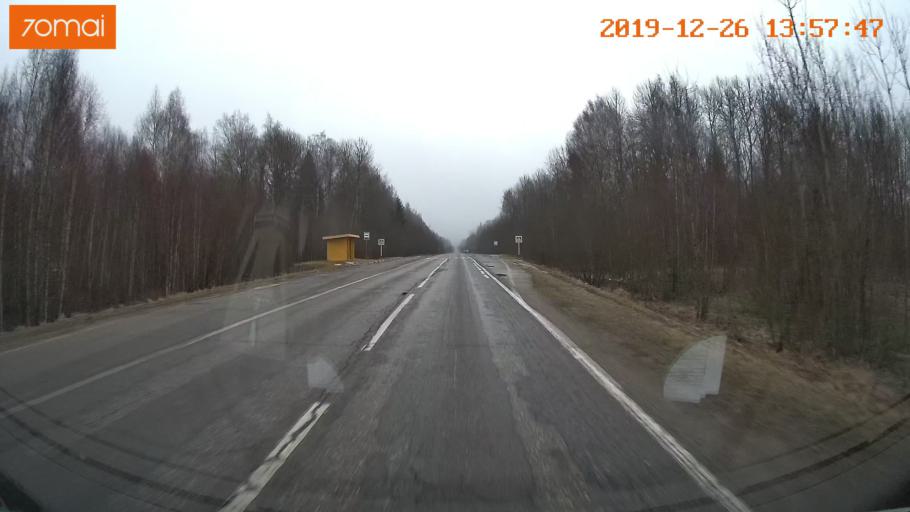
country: RU
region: Jaroslavl
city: Poshekhon'ye
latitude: 58.5793
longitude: 38.6869
